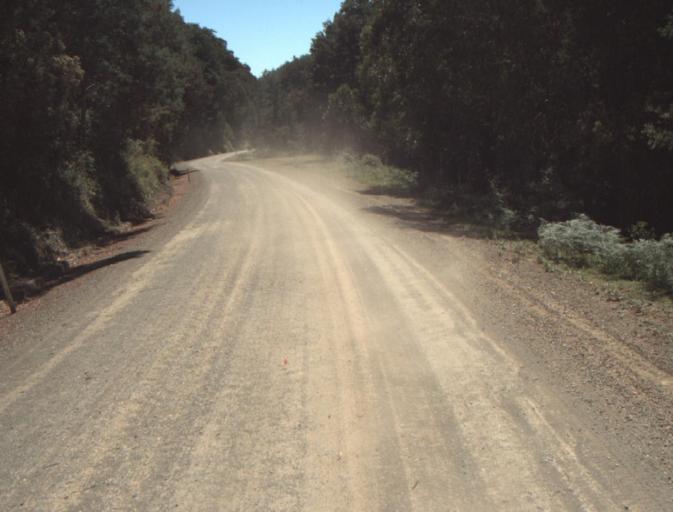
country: AU
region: Tasmania
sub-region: Dorset
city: Scottsdale
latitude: -41.3264
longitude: 147.4235
